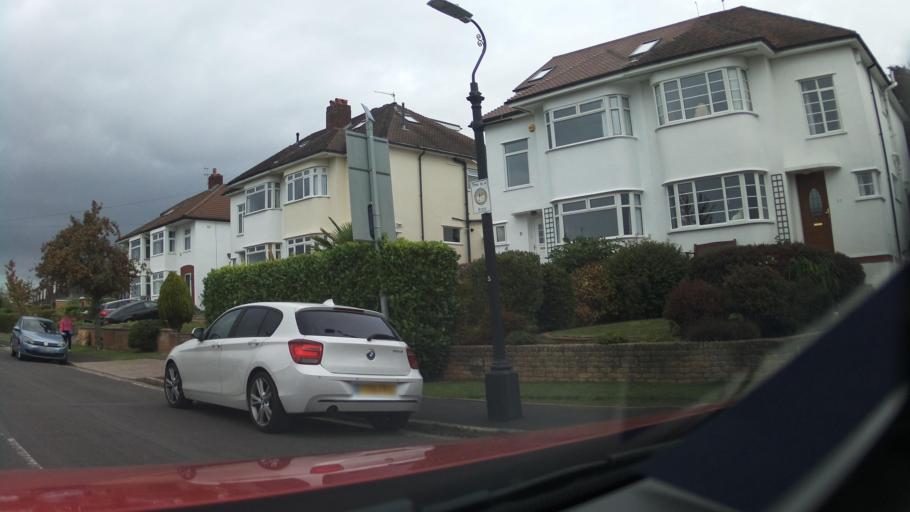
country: GB
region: England
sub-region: Bristol
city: Bristol
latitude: 51.4873
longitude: -2.6240
